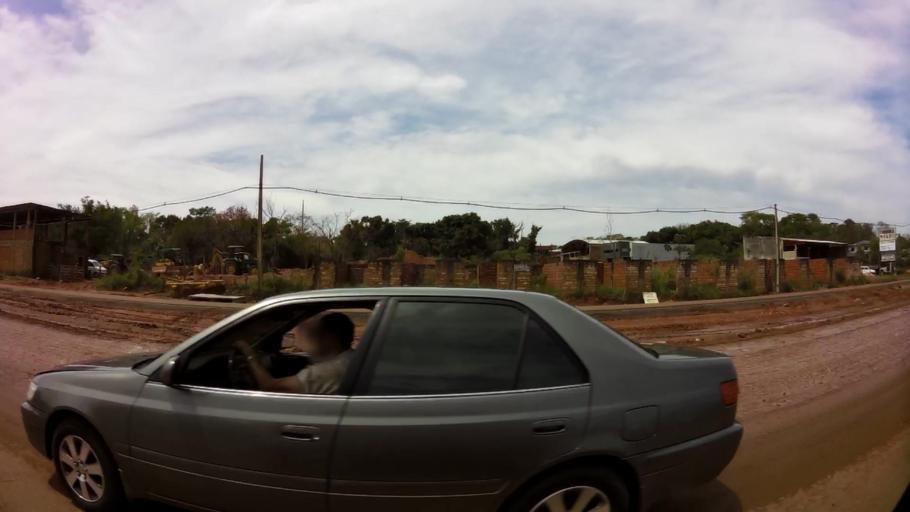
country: PY
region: Central
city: Colonia Mariano Roque Alonso
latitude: -25.2003
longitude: -57.5206
